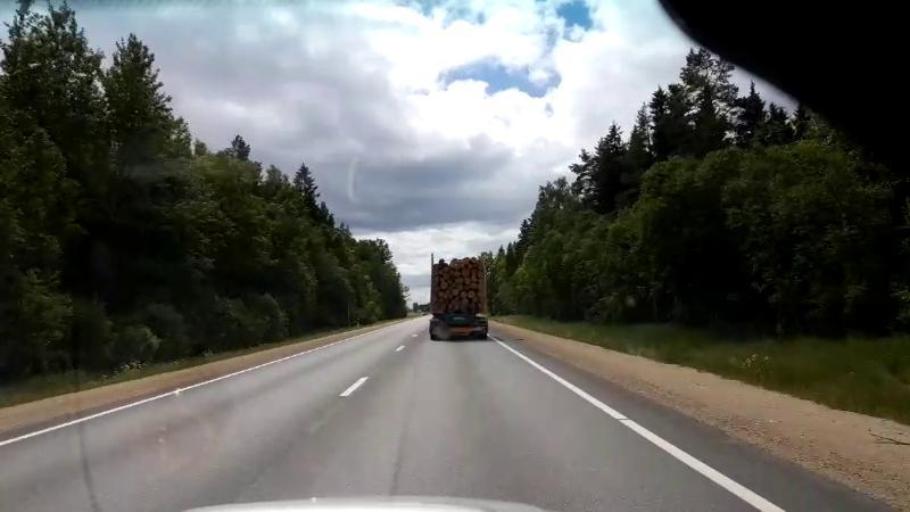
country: LV
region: Salacgrivas
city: Salacgriva
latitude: 57.7098
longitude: 24.3673
